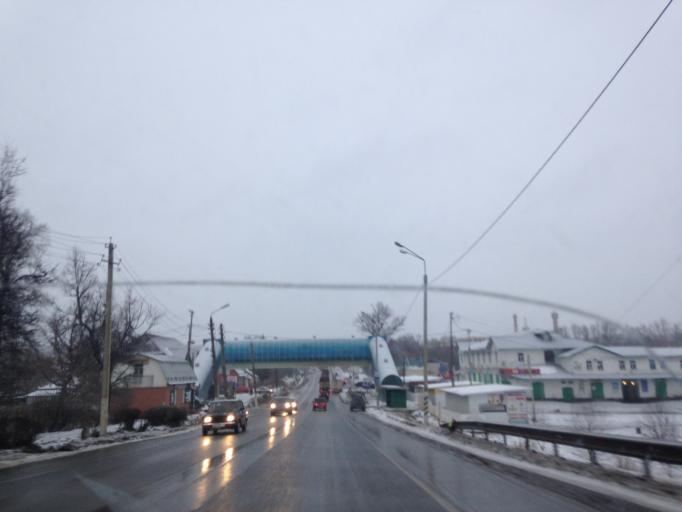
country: RU
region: Tula
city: Plavsk
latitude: 53.7090
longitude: 37.2948
